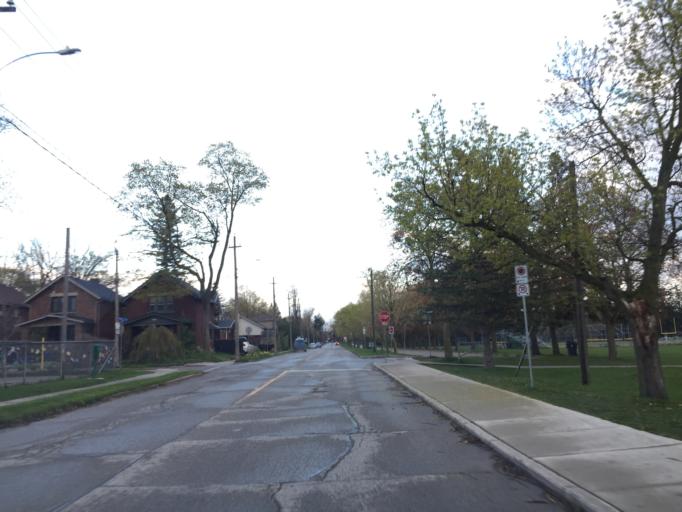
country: CA
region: Ontario
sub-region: Wellington County
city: Guelph
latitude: 43.5516
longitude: -80.2637
